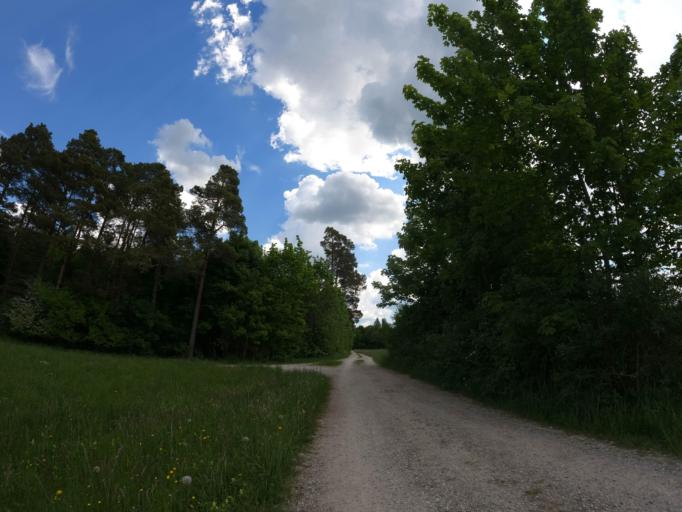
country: DE
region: Bavaria
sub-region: Upper Bavaria
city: Sauerlach
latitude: 47.9834
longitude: 11.6690
